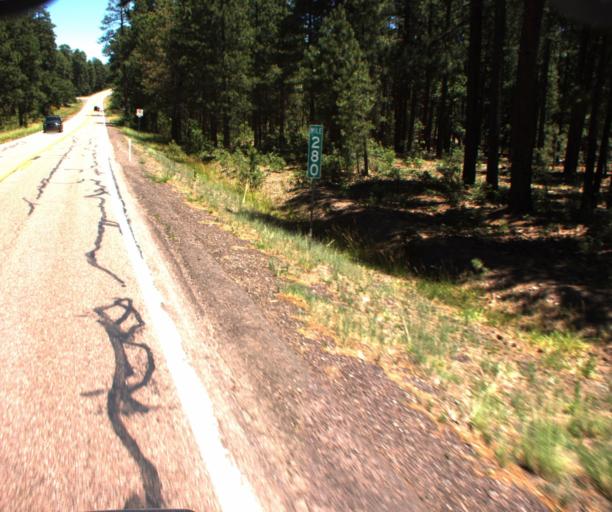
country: US
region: Arizona
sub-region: Gila County
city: Pine
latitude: 34.4538
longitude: -111.4152
